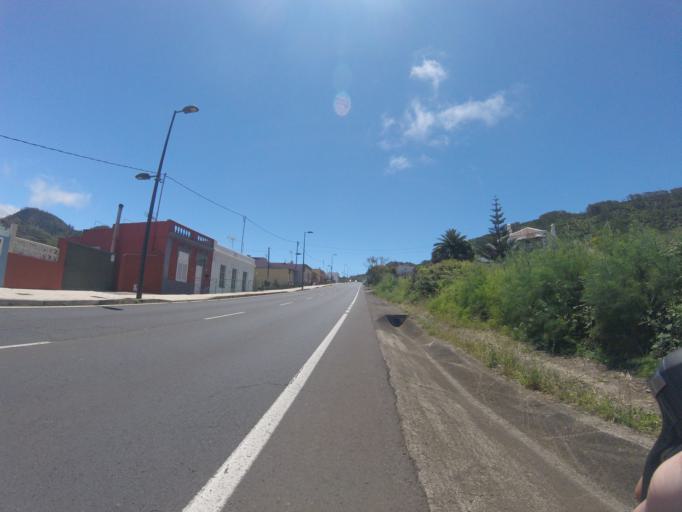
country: ES
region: Canary Islands
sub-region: Provincia de Santa Cruz de Tenerife
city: Tegueste
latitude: 28.5166
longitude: -16.3197
